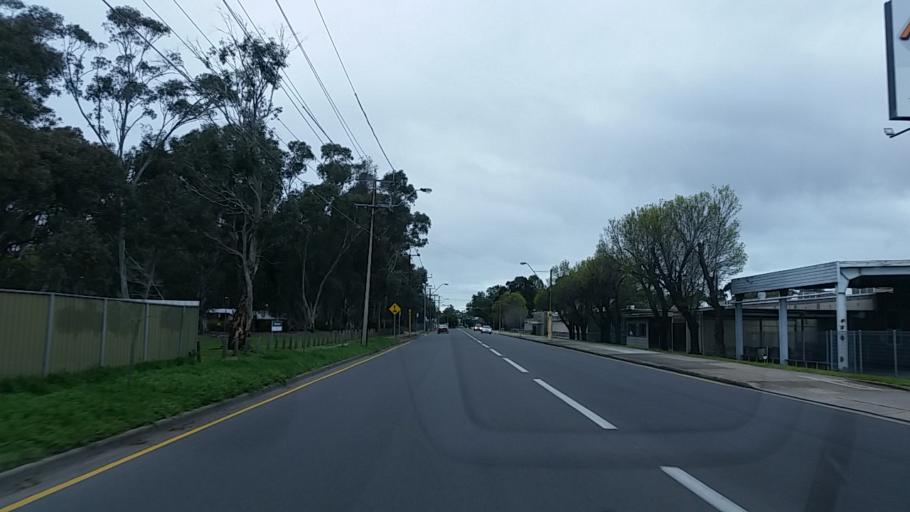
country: AU
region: South Australia
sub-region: Charles Sturt
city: Findon
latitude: -34.9159
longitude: 138.5347
